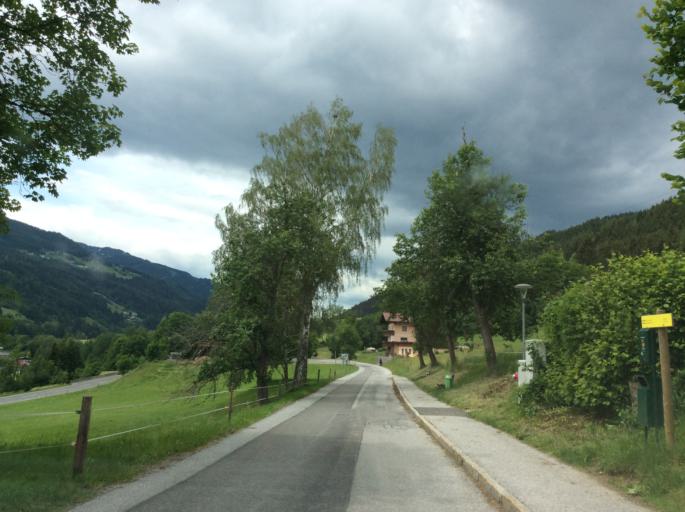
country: AT
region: Styria
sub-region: Politischer Bezirk Liezen
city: Schladming
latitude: 47.3971
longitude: 13.6806
